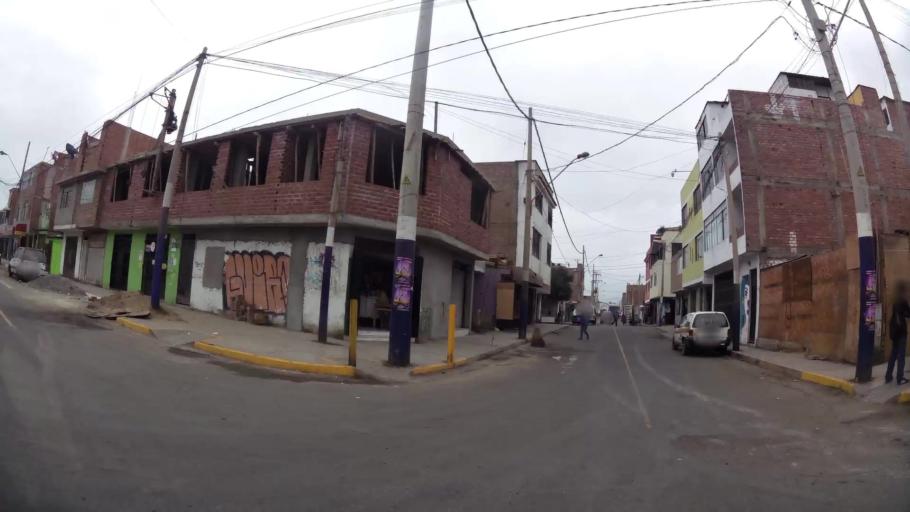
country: PE
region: Lima
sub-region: Lima
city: Surco
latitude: -12.1977
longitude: -76.9961
